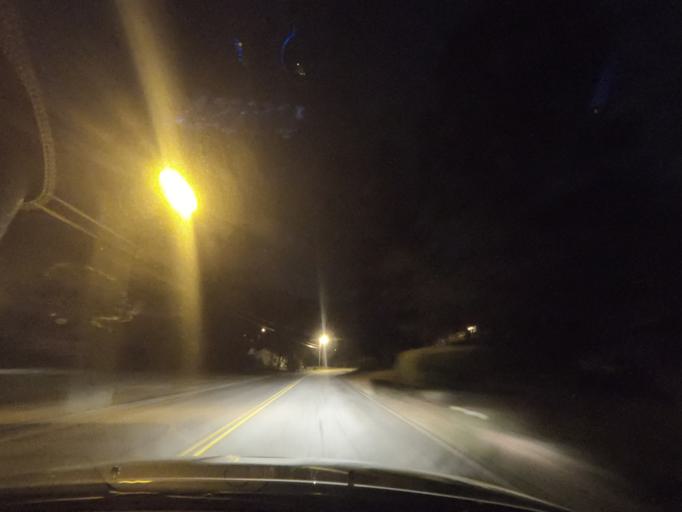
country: US
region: Georgia
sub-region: Fulton County
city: College Park
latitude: 33.6712
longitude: -84.4763
